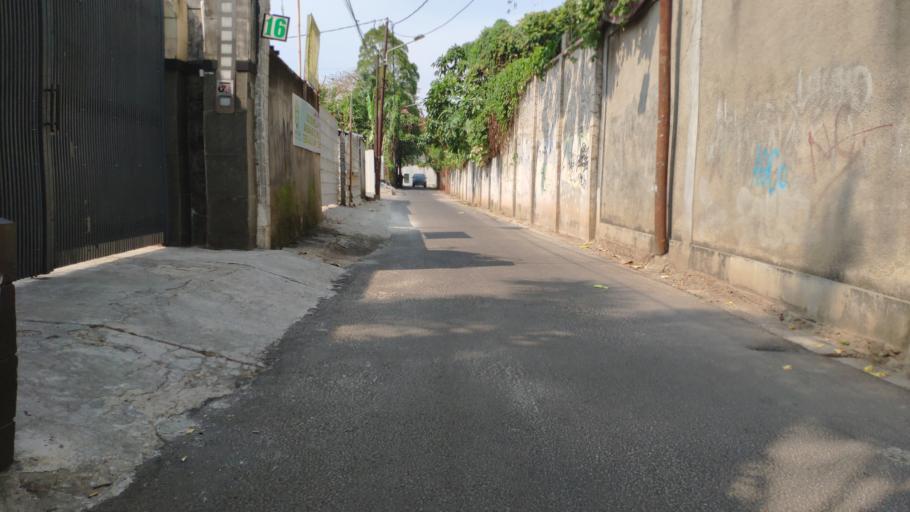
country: ID
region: Jakarta Raya
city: Jakarta
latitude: -6.2732
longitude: 106.8241
